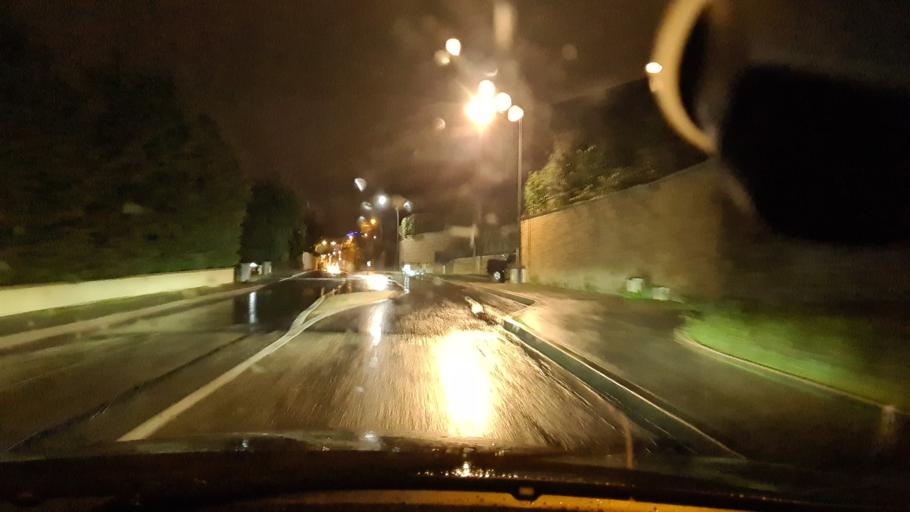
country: FR
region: Rhone-Alpes
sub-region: Departement du Rhone
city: Limonest
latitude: 45.8083
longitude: 4.7912
